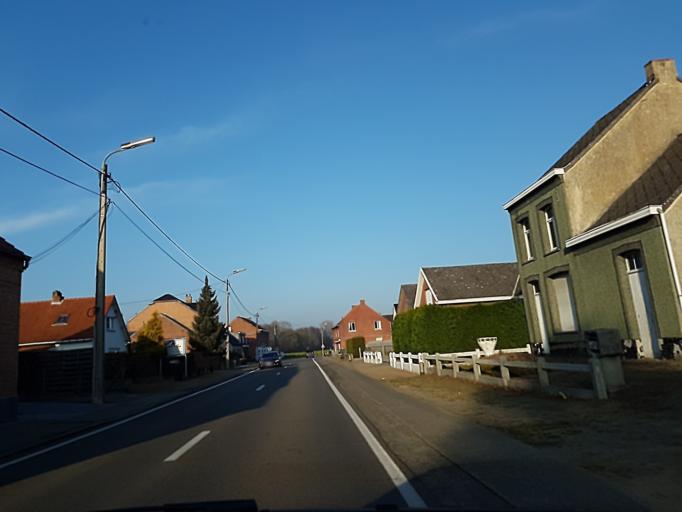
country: BE
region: Flanders
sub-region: Provincie Vlaams-Brabant
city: Tremelo
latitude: 51.0010
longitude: 4.7066
